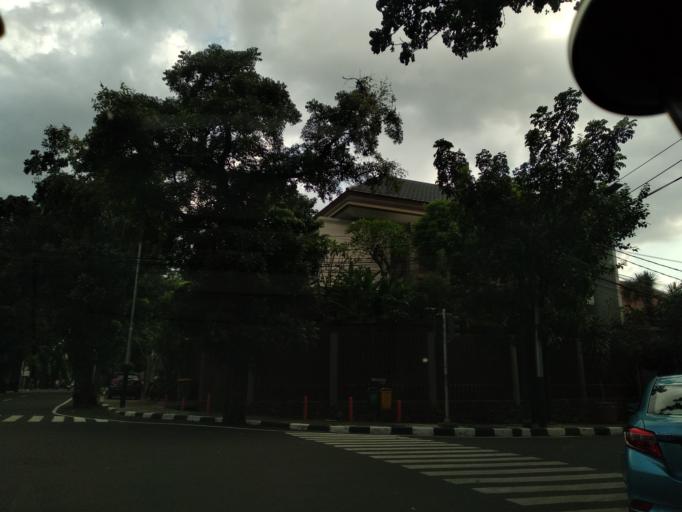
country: ID
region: Jakarta Raya
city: Jakarta
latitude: -6.2330
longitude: 106.7975
